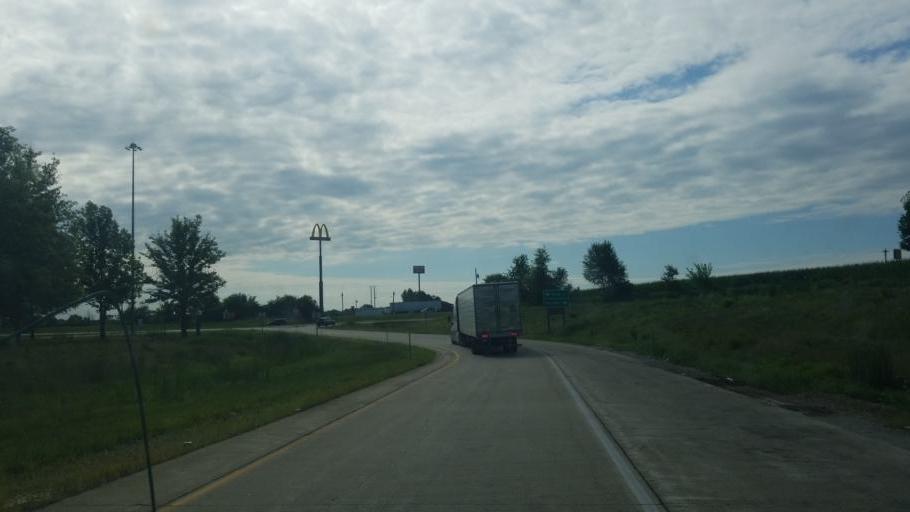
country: US
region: Illinois
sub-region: Clark County
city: Marshall
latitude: 39.4200
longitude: -87.6952
